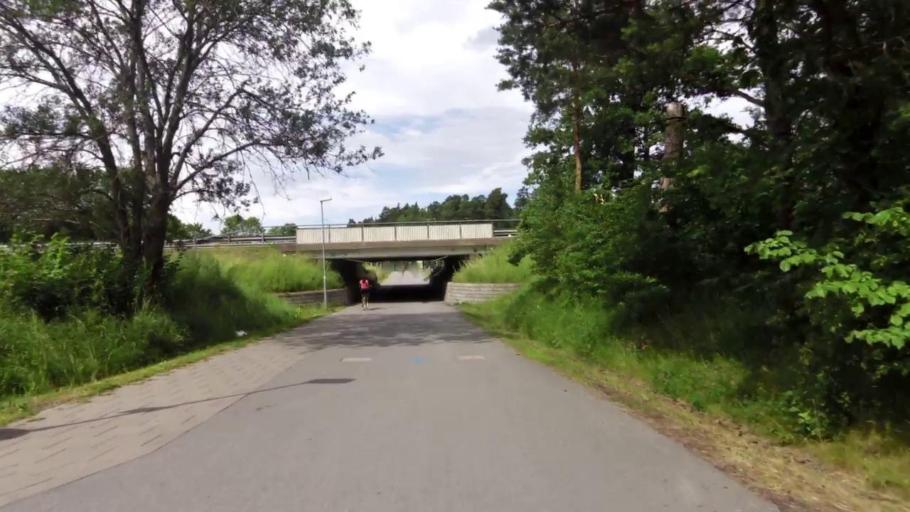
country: SE
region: OEstergoetland
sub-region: Linkopings Kommun
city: Linkoping
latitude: 58.4053
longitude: 15.5780
